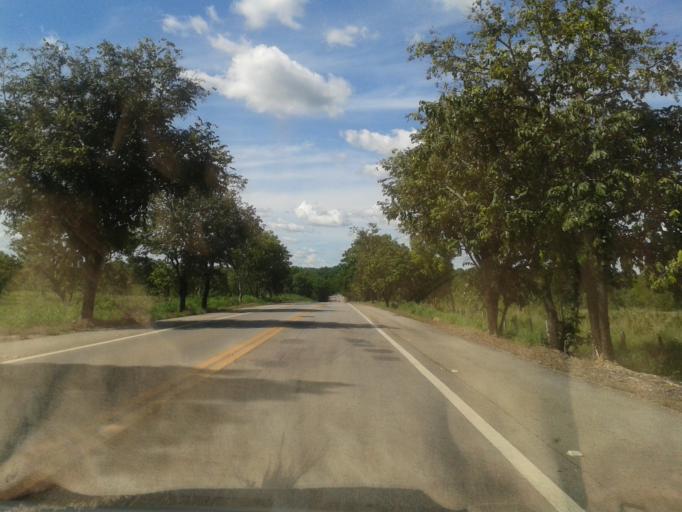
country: BR
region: Goias
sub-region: Itapuranga
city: Itapuranga
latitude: -15.4128
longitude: -50.3778
